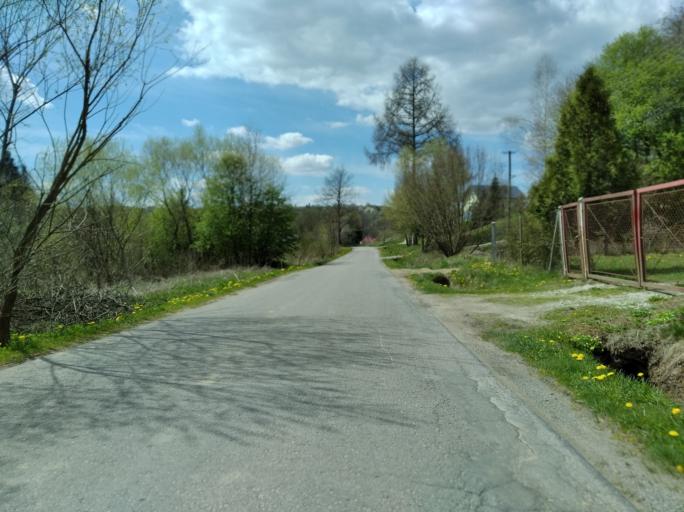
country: PL
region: Subcarpathian Voivodeship
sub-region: Powiat brzozowski
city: Wesola
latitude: 49.7537
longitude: 22.1199
